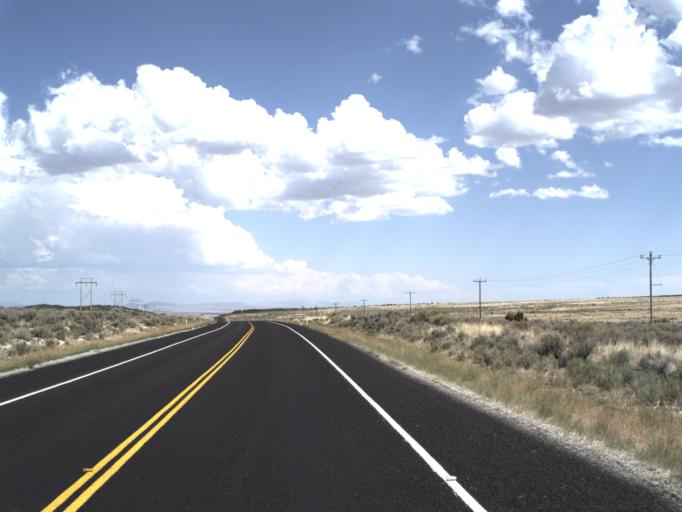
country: US
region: Idaho
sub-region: Minidoka County
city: Rupert
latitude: 41.9934
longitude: -113.1880
